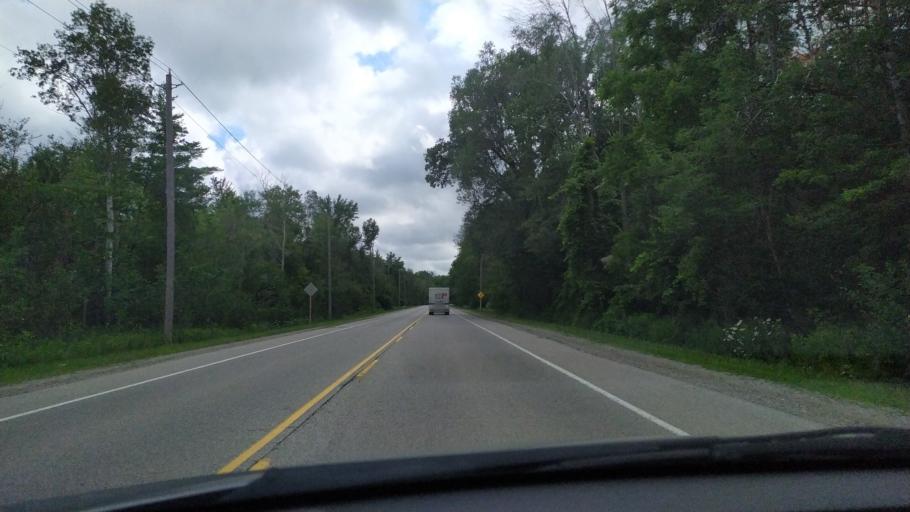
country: CA
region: Ontario
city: Kitchener
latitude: 43.3704
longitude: -80.4285
